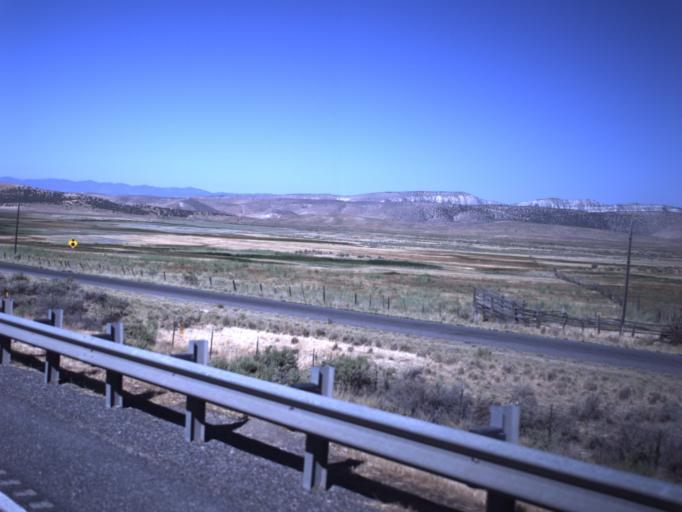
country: US
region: Utah
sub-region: Sanpete County
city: Manti
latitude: 39.2401
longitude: -111.6561
